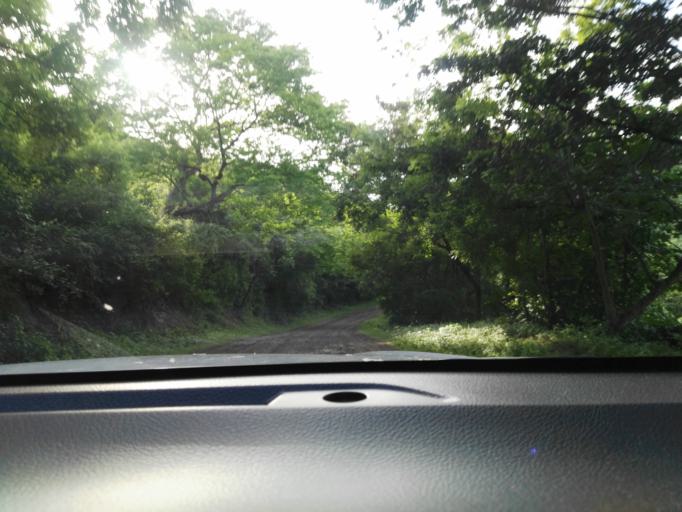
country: NI
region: Matagalpa
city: Terrabona
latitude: 12.8452
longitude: -86.0328
